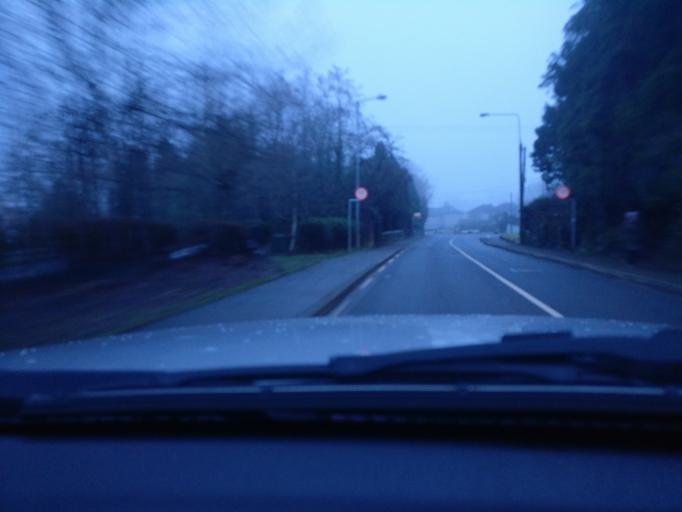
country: IE
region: Leinster
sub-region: An Mhi
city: Athboy
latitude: 53.6185
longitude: -6.9273
